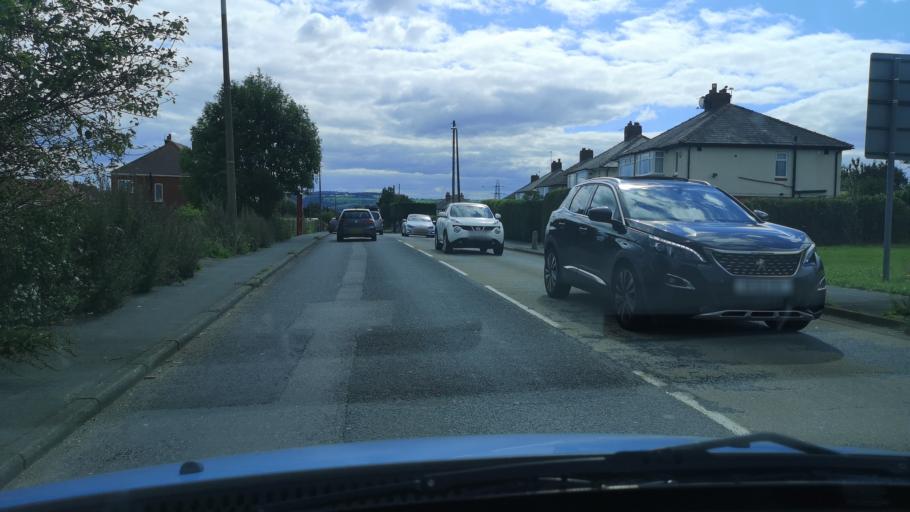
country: GB
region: England
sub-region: Kirklees
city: Liversedge
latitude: 53.6958
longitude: -1.6995
